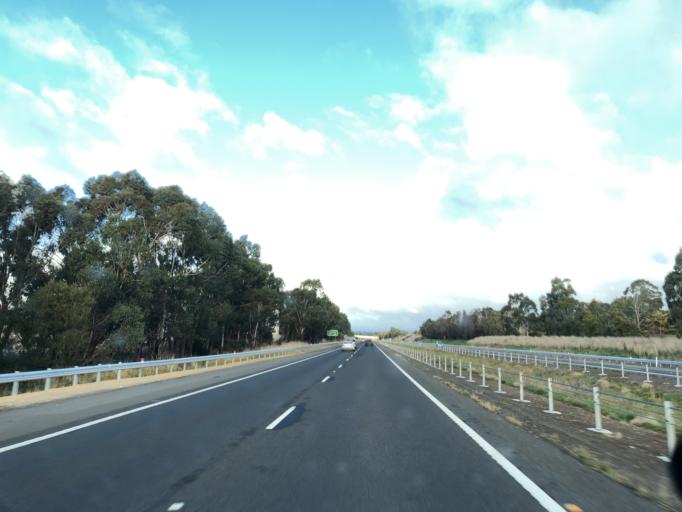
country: AU
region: Victoria
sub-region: Mount Alexander
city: Castlemaine
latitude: -37.2327
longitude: 144.4485
